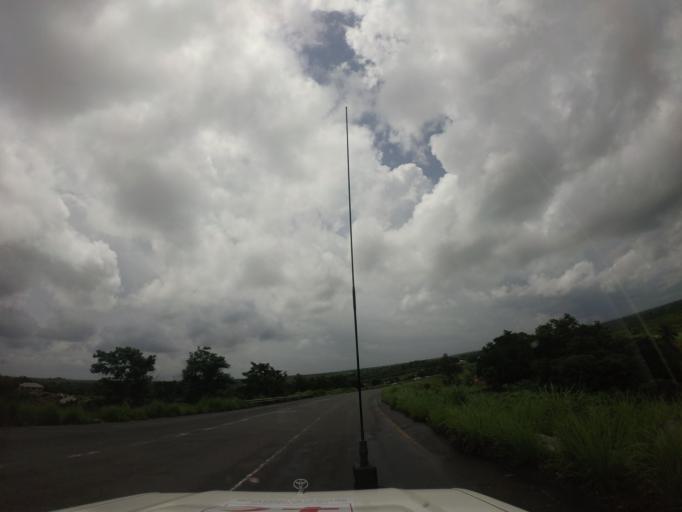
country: SL
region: Northern Province
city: Pepel
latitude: 8.4676
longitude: -12.8328
